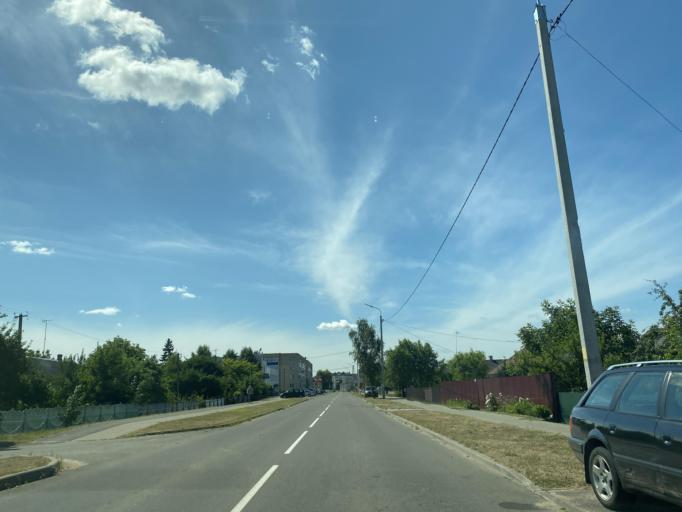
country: BY
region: Brest
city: Ivanava
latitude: 52.1535
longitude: 25.5435
